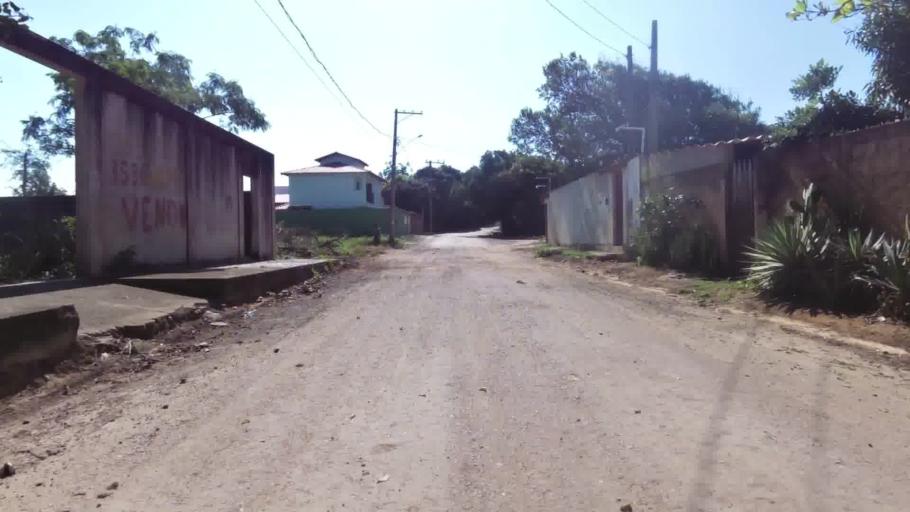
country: BR
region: Espirito Santo
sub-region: Piuma
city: Piuma
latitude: -20.8286
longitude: -40.6206
